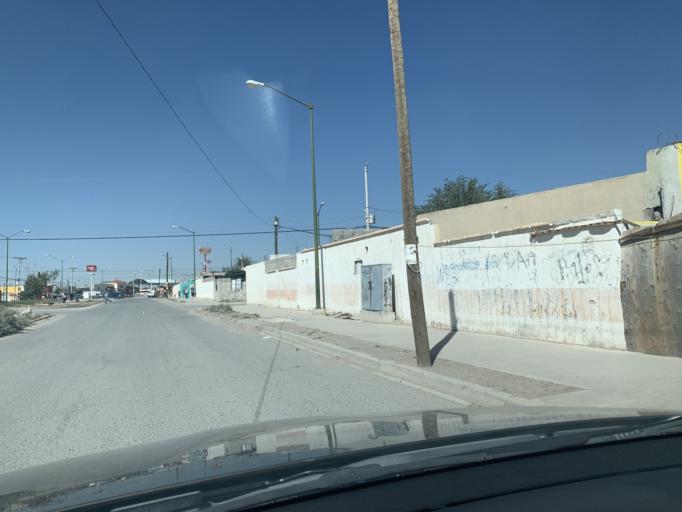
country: US
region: Texas
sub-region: El Paso County
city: Socorro Mission Number 1 Colonia
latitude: 31.5940
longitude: -106.3583
